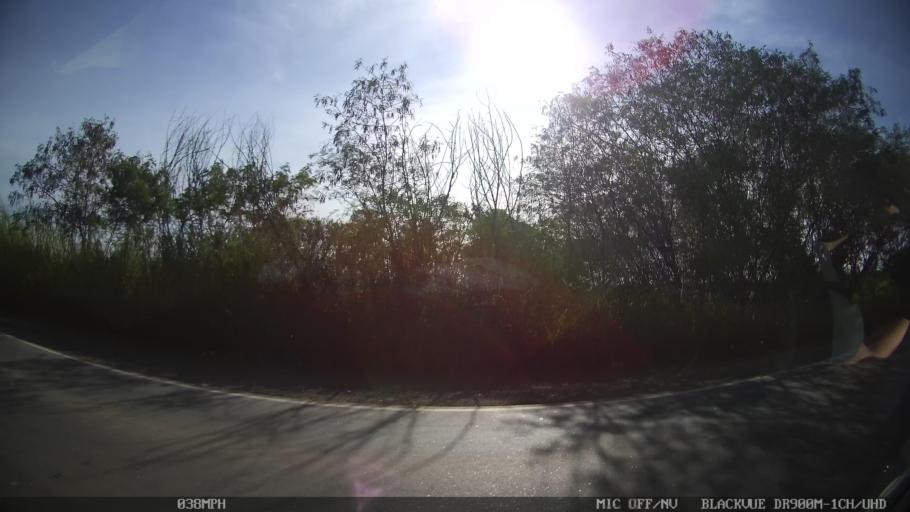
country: BR
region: Sao Paulo
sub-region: Rio Das Pedras
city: Rio das Pedras
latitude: -22.7915
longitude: -47.6255
